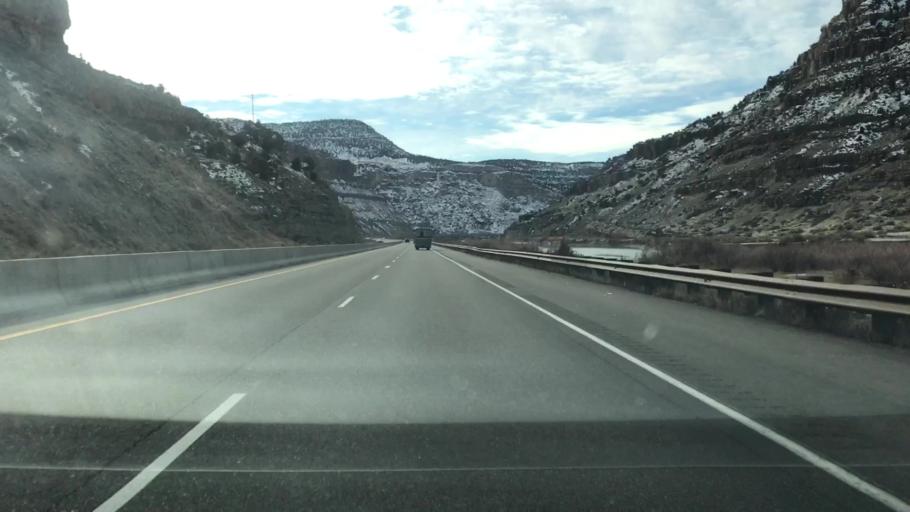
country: US
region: Colorado
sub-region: Mesa County
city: Palisade
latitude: 39.2214
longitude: -108.2561
